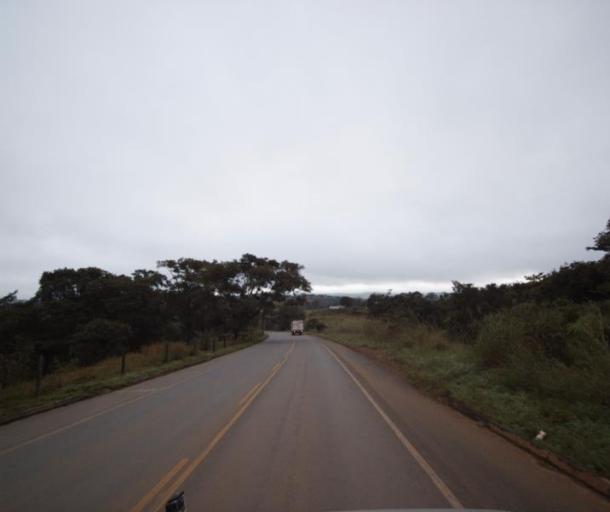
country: BR
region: Goias
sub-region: Pirenopolis
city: Pirenopolis
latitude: -15.9533
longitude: -48.8061
